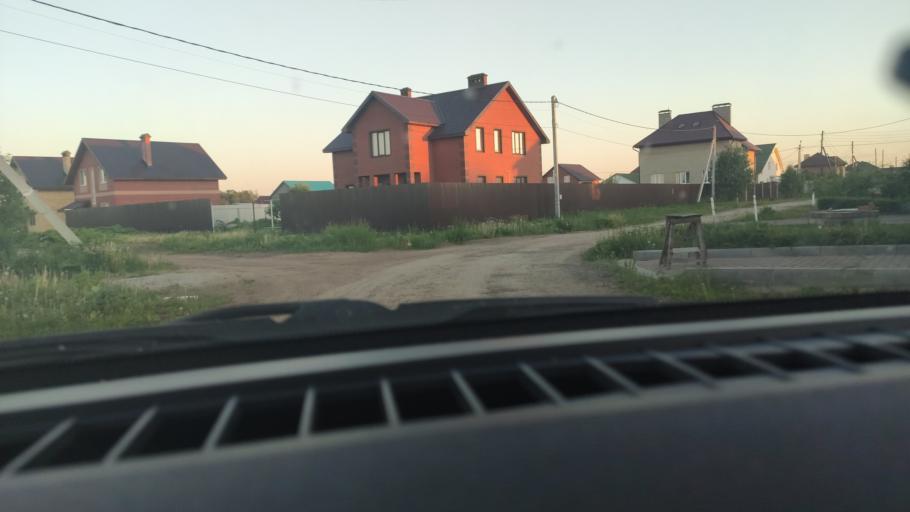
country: RU
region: Perm
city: Kultayevo
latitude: 57.9017
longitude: 55.9721
